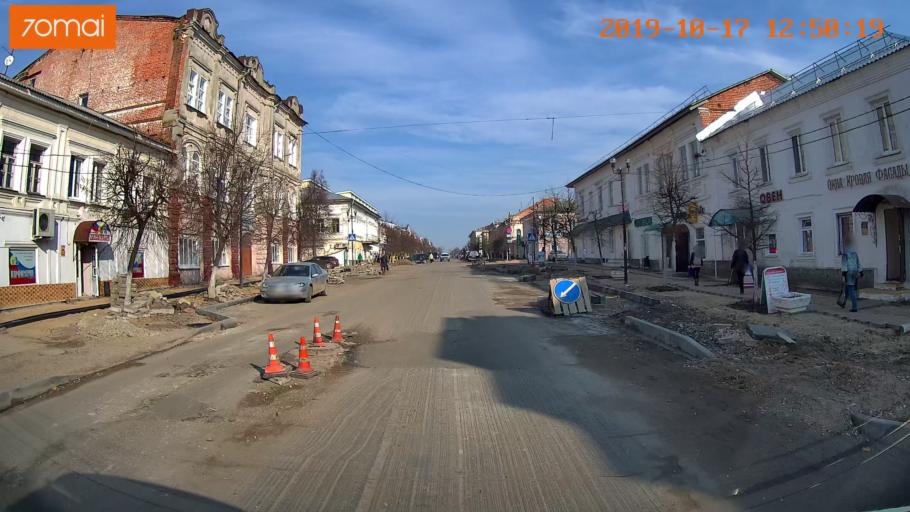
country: RU
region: Rjazan
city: Kasimov
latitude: 54.9378
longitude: 41.3924
